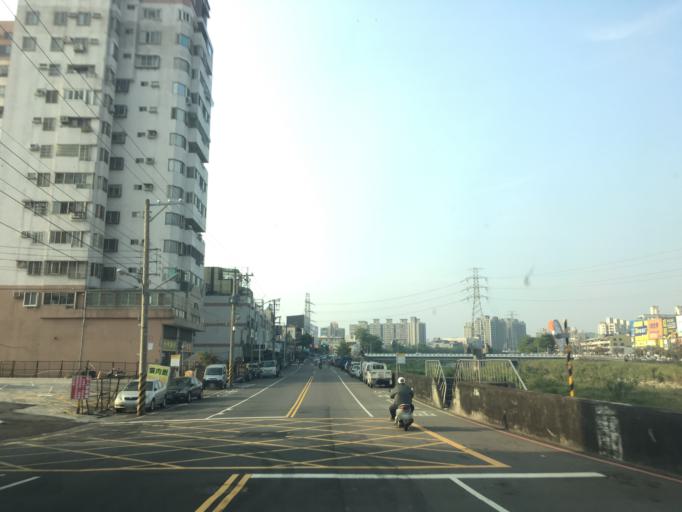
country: TW
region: Taiwan
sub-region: Taichung City
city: Taichung
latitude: 24.1451
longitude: 120.6997
